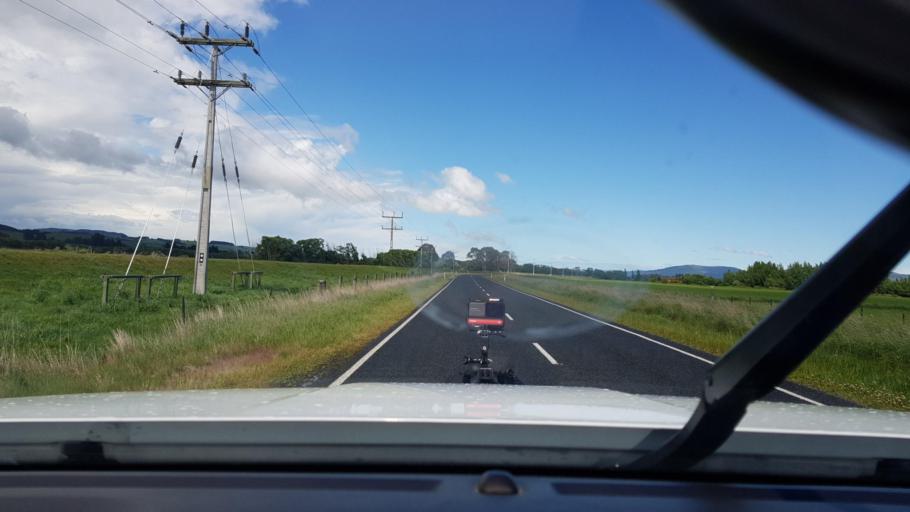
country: NZ
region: Southland
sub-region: Southland District
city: Winton
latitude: -45.8369
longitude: 168.3703
